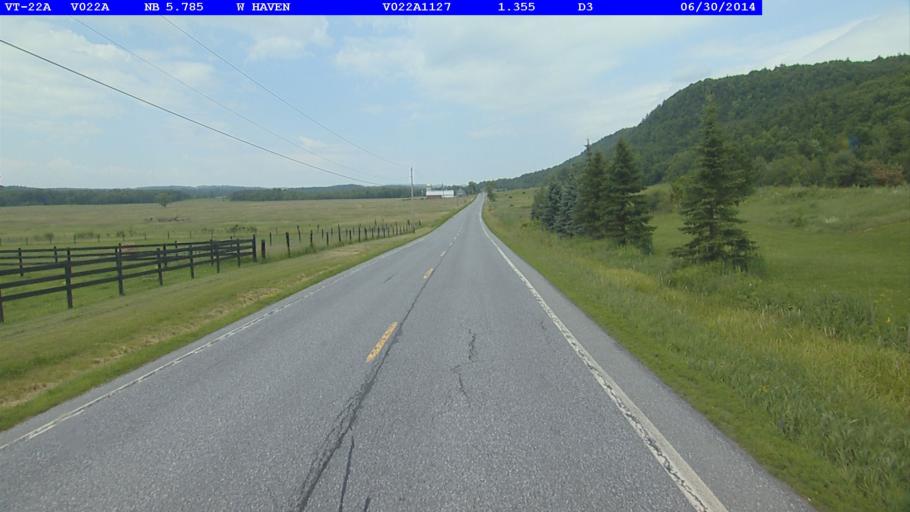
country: US
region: Vermont
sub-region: Rutland County
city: Fair Haven
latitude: 43.6470
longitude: -73.2967
